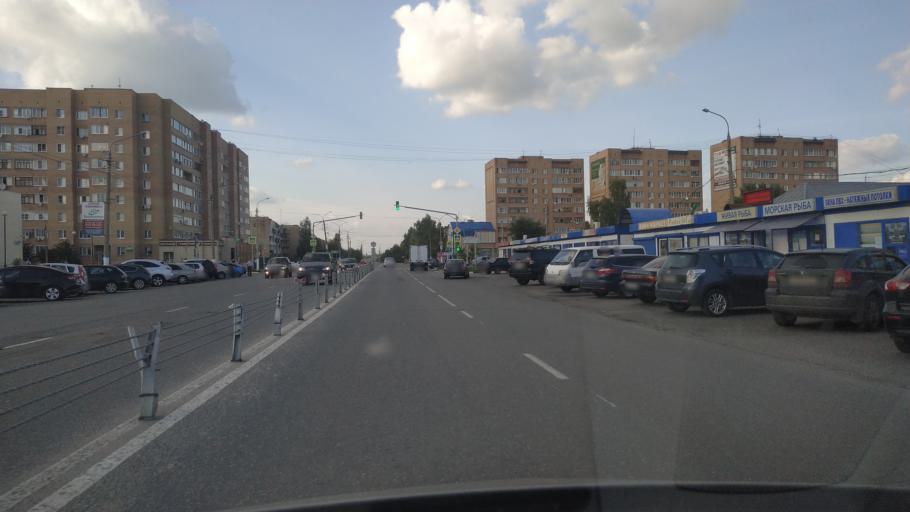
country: RU
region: Moskovskaya
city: Shatura
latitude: 55.5763
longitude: 39.5210
